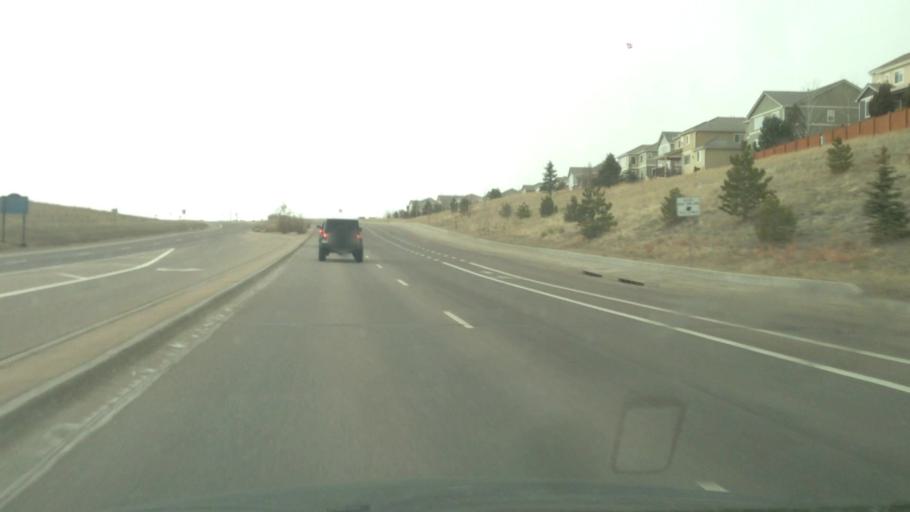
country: US
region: Colorado
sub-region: Douglas County
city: Stonegate
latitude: 39.4930
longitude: -104.8022
